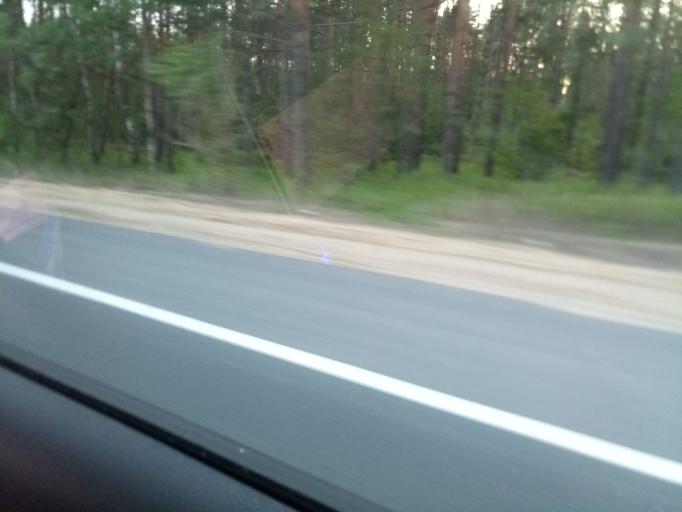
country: RU
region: Moskovskaya
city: Noginsk-9
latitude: 56.0999
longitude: 38.5843
